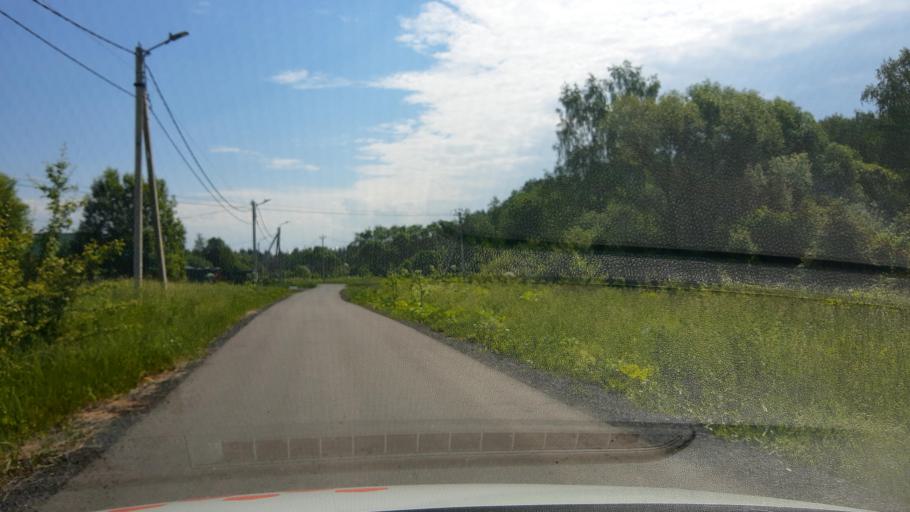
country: RU
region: Moskovskaya
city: Kievskij
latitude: 55.2235
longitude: 36.9834
